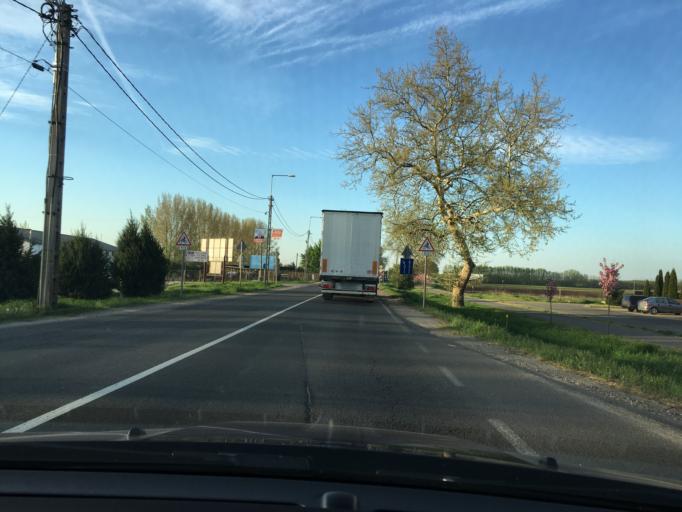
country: HU
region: Hajdu-Bihar
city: Mikepercs
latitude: 47.4497
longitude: 21.6328
